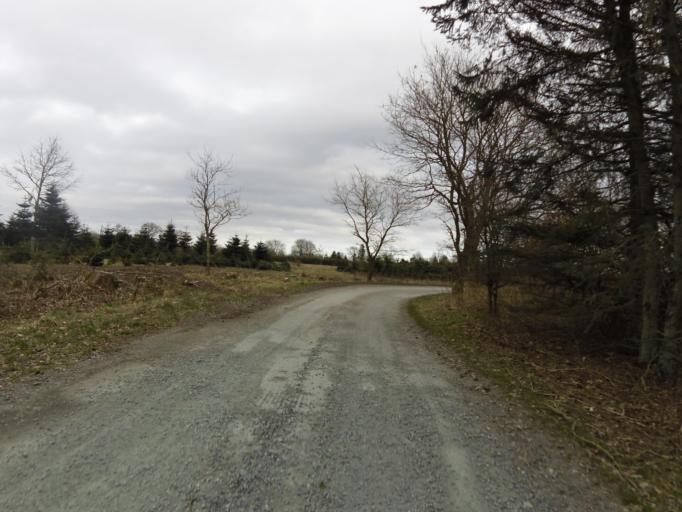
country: DK
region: South Denmark
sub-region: Tonder Kommune
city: Toftlund
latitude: 55.2109
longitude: 9.1738
